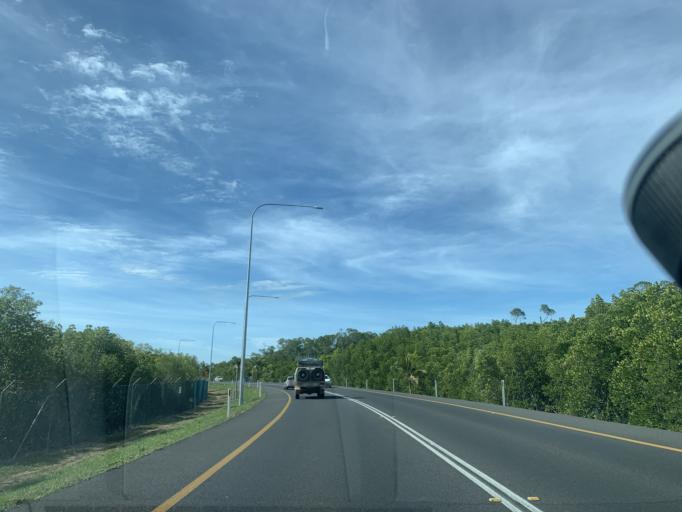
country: AU
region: Queensland
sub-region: Cairns
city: Cairns
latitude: -16.8873
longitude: 145.7624
